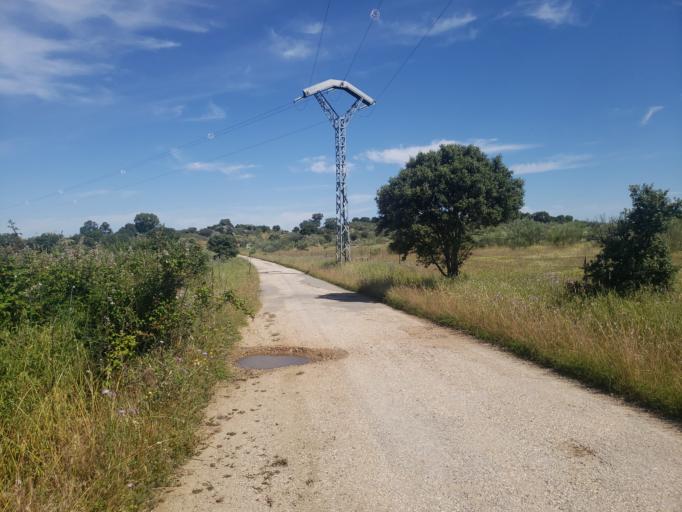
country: ES
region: Extremadura
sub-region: Provincia de Caceres
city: Malpartida de Caceres
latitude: 39.4157
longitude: -6.5007
